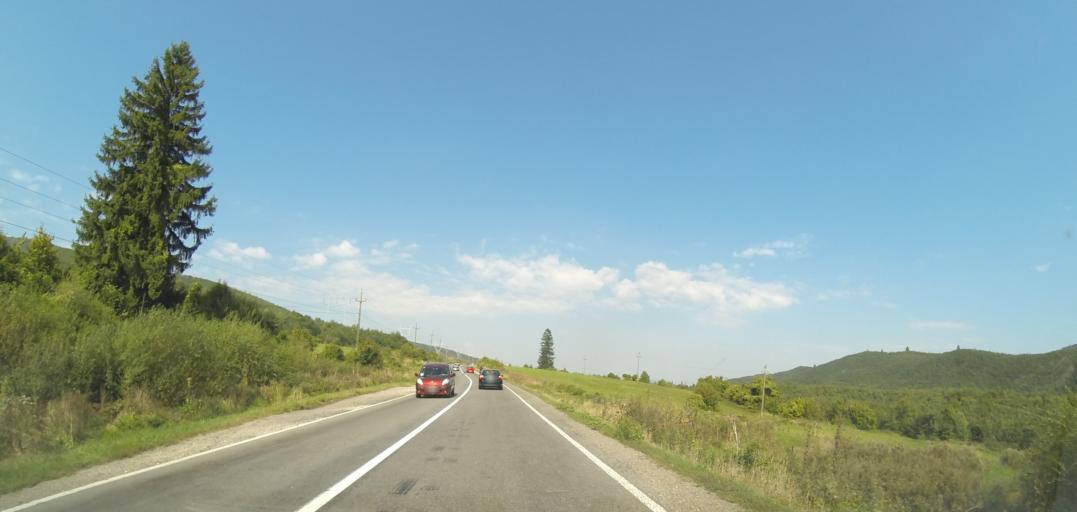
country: RO
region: Brasov
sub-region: Comuna Tarlungeni
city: Tarlungeni
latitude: 45.5877
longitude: 25.7552
